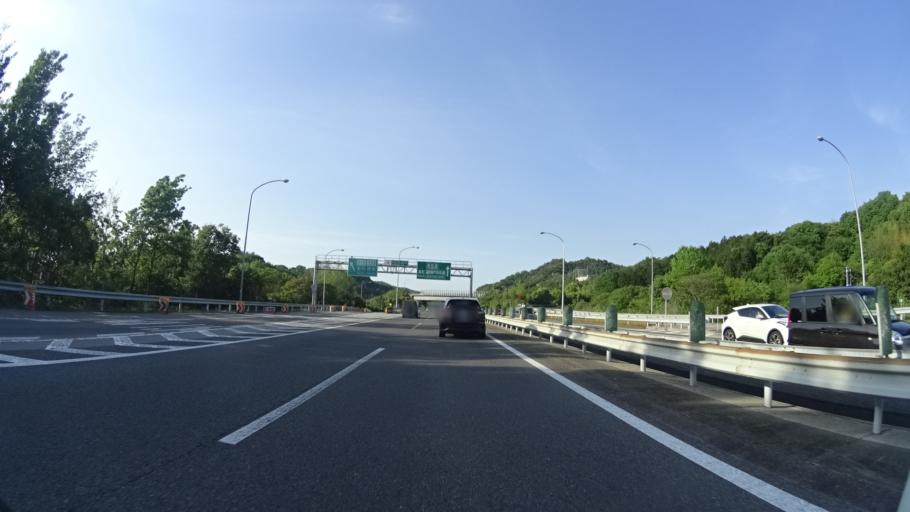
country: JP
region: Ehime
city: Kawanoecho
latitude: 33.9983
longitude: 133.5964
